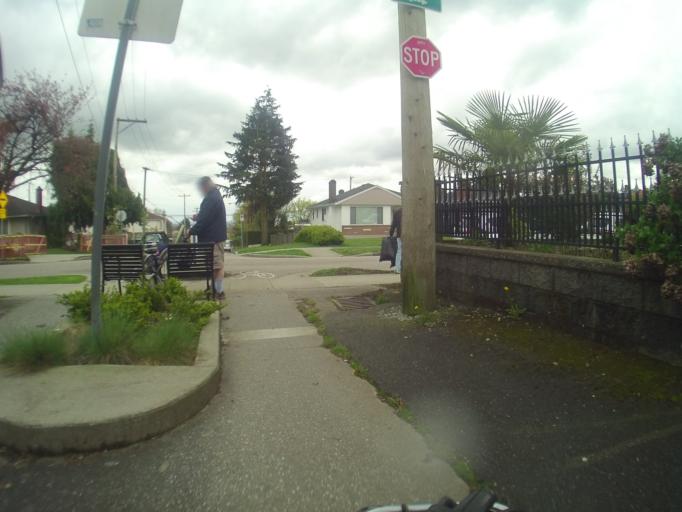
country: CA
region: British Columbia
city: Vancouver
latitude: 49.2165
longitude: -123.0740
